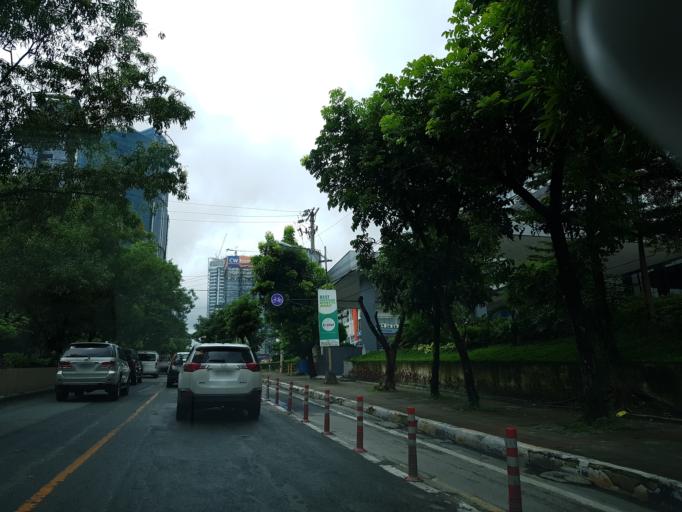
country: PH
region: Metro Manila
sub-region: Pasig
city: Pasig City
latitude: 14.5844
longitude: 121.0667
